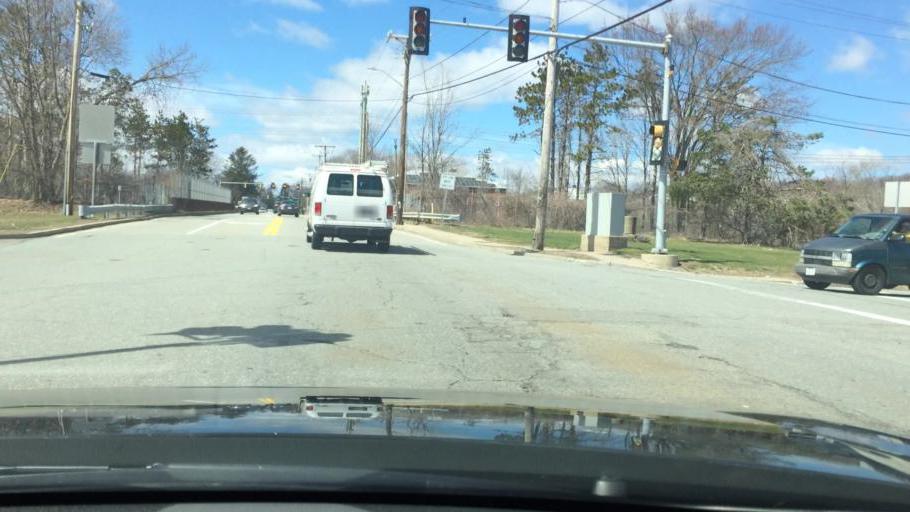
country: US
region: Massachusetts
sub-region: Essex County
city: Methuen
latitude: 42.7418
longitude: -71.1682
